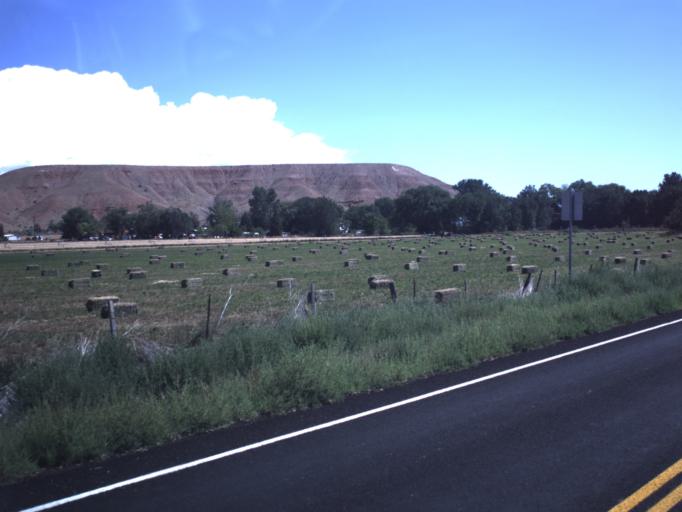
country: US
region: Utah
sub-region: Duchesne County
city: Roosevelt
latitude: 40.4037
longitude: -109.8012
